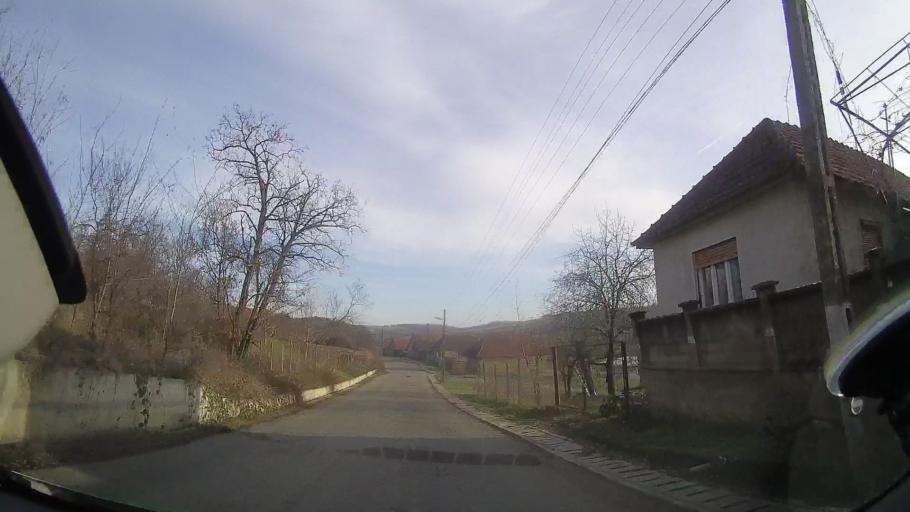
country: RO
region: Bihor
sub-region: Comuna Sarbi
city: Burzuc
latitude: 47.1487
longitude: 22.1755
